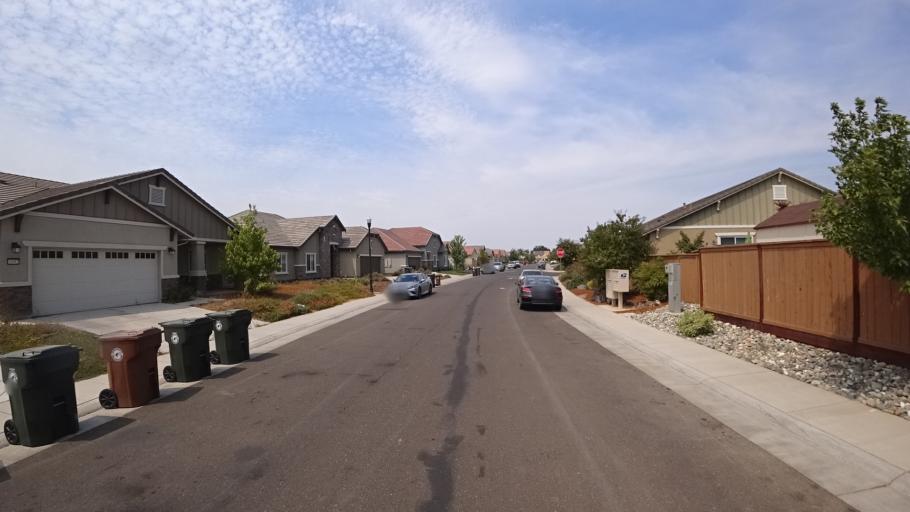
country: US
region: California
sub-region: Sacramento County
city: Laguna
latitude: 38.3914
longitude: -121.4139
